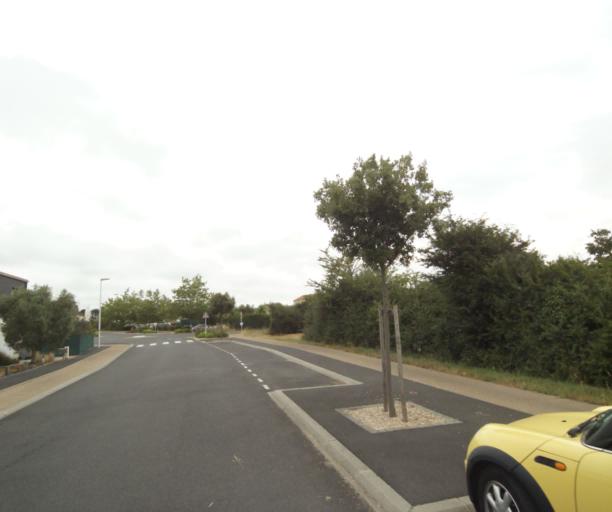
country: FR
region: Pays de la Loire
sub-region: Departement de la Vendee
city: Chateau-d'Olonne
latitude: 46.4764
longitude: -1.7375
